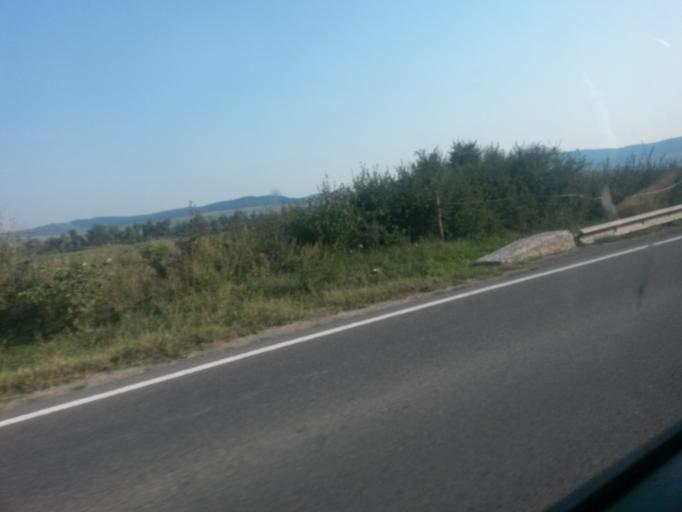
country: RO
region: Alba
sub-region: Comuna Unirea
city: Unirea
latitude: 46.3939
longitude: 23.7926
